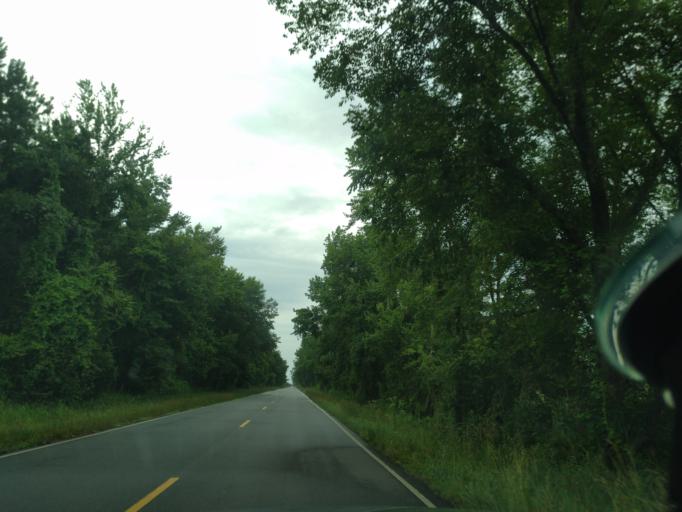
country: US
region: North Carolina
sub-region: Washington County
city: Plymouth
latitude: 35.8560
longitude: -76.5715
